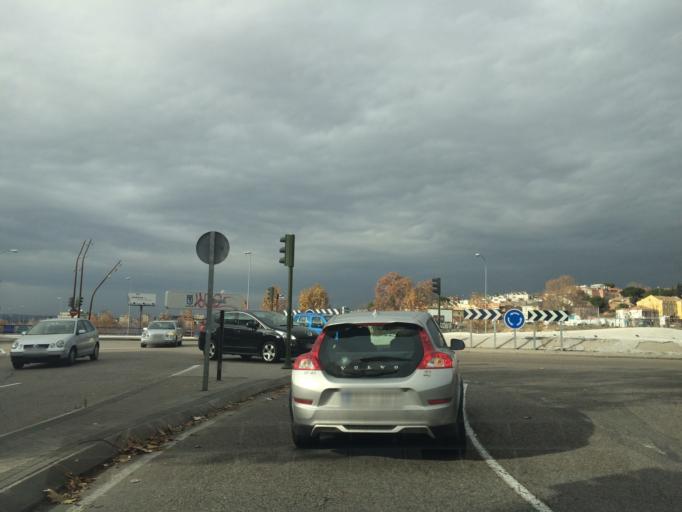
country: ES
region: Madrid
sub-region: Provincia de Madrid
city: Tetuan de las Victorias
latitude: 40.4726
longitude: -3.7280
